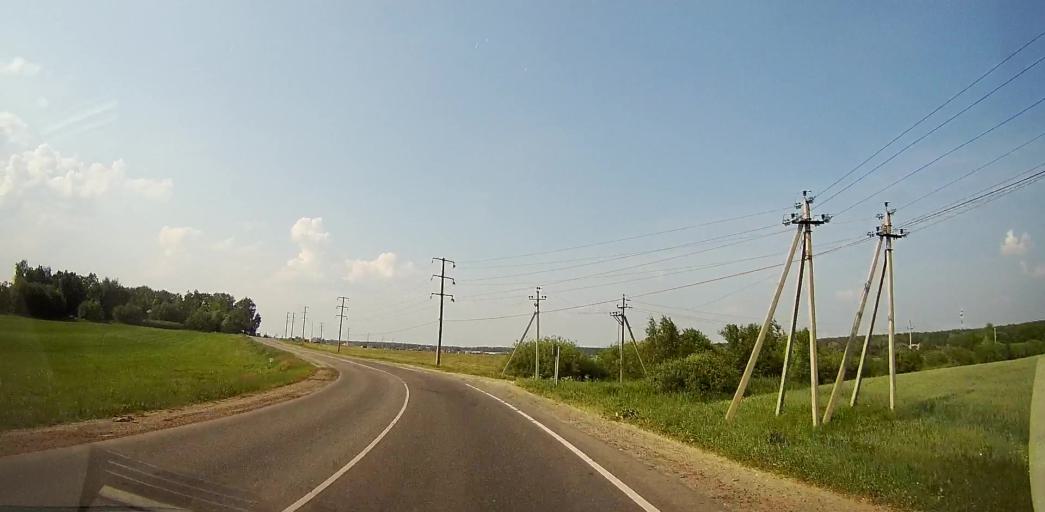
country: RU
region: Moskovskaya
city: Barybino
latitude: 55.2614
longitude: 37.9190
